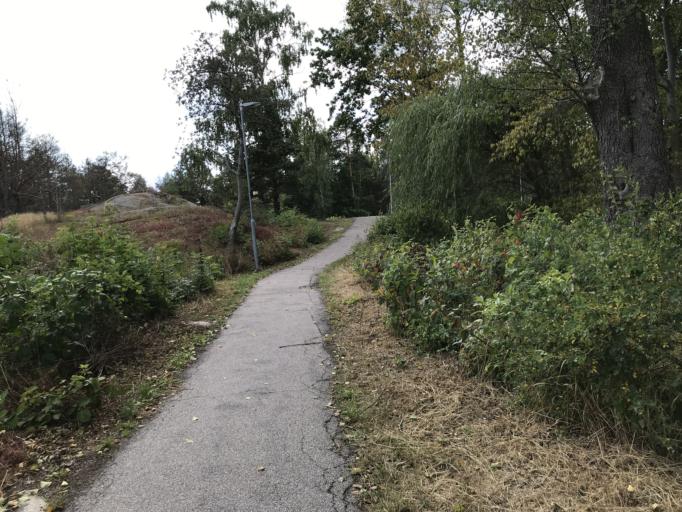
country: SE
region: Kalmar
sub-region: Oskarshamns Kommun
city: Oskarshamn
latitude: 57.2619
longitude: 16.4568
